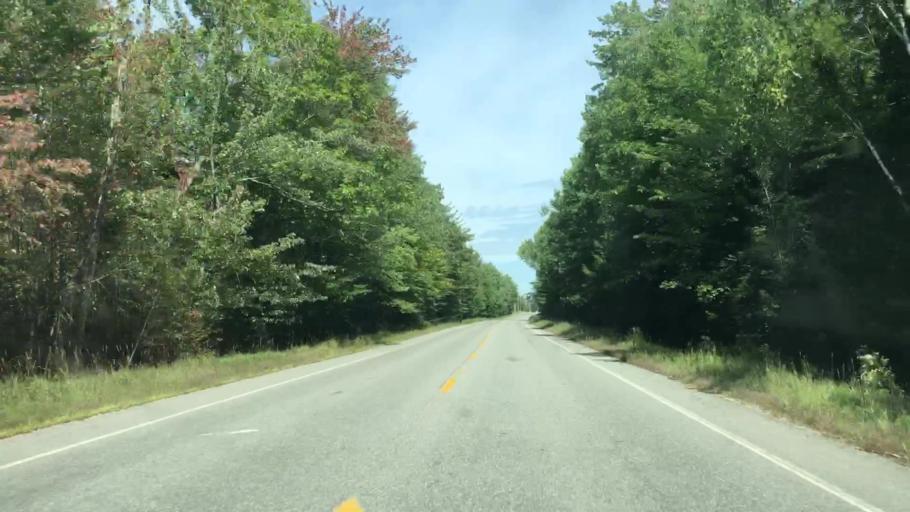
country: US
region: Maine
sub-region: Penobscot County
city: Lincoln
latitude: 45.3865
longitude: -68.5384
